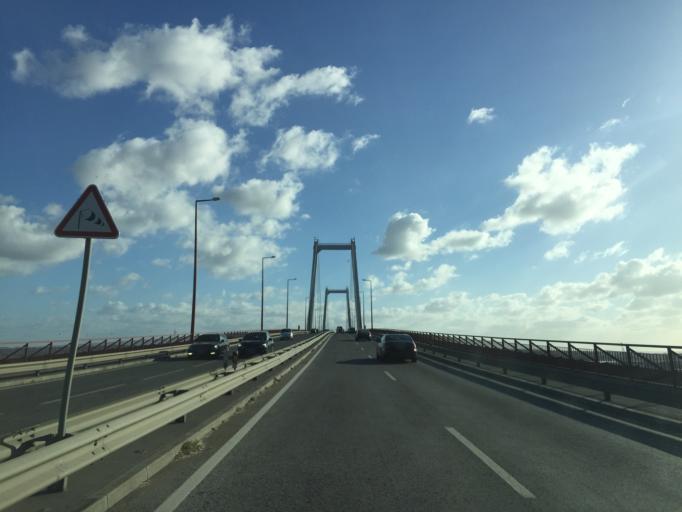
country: PT
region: Coimbra
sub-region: Figueira da Foz
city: Figueira da Foz
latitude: 40.1488
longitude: -8.8417
